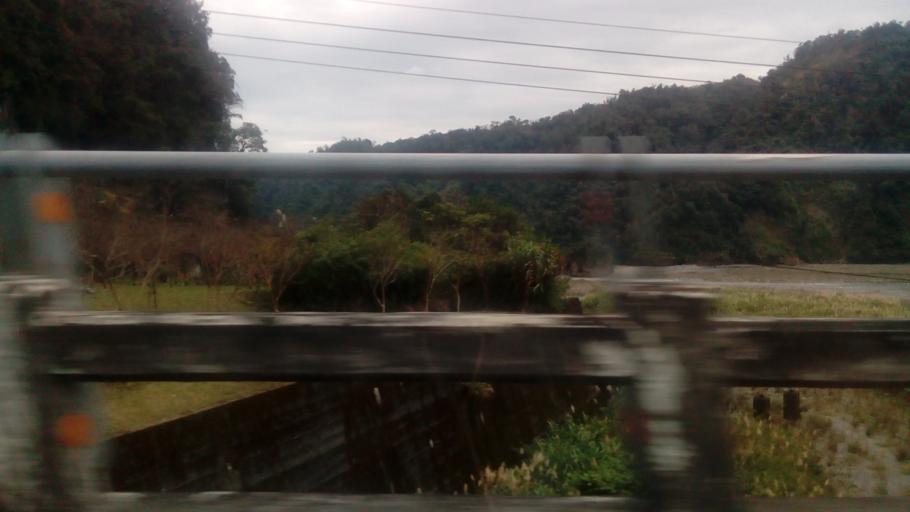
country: TW
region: Taiwan
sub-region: Yilan
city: Yilan
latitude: 24.6385
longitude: 121.5539
